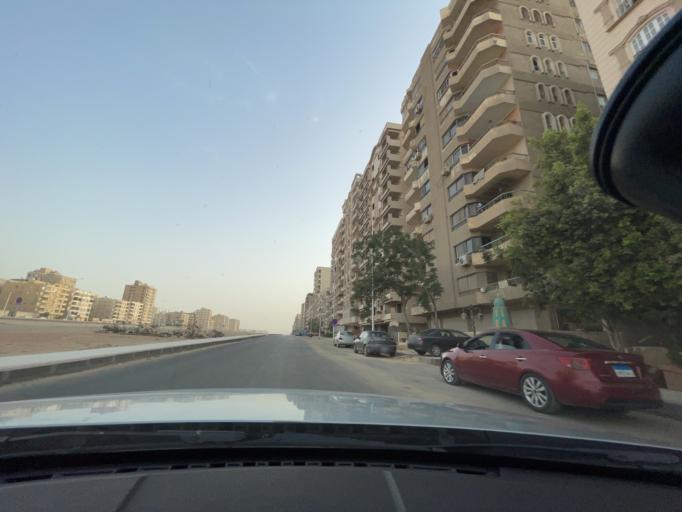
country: EG
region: Muhafazat al Qahirah
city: Cairo
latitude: 30.0550
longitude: 31.3720
